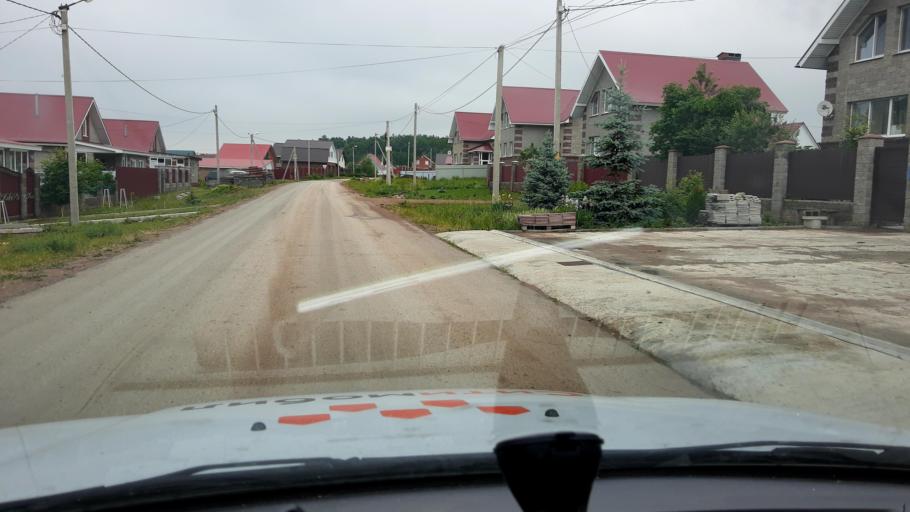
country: RU
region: Bashkortostan
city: Kabakovo
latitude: 54.6651
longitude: 56.2188
